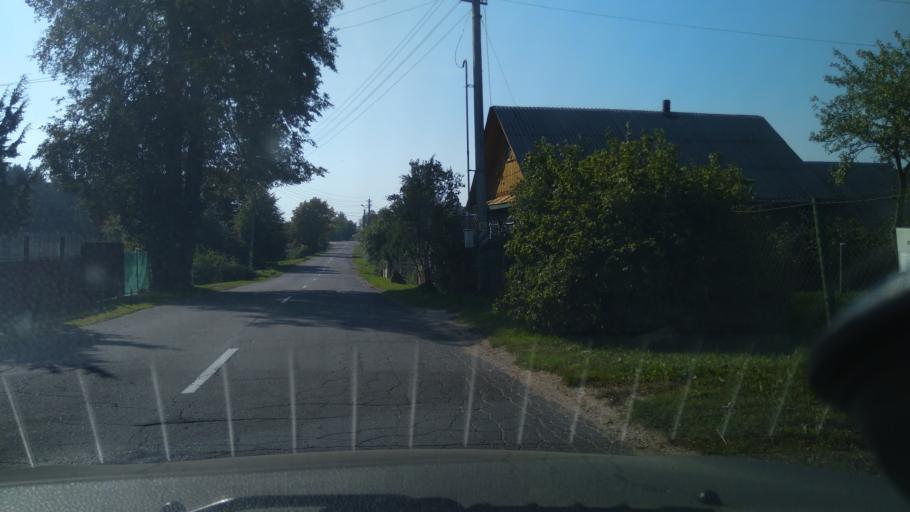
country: BY
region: Minsk
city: Rakaw
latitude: 54.0059
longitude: 27.0477
